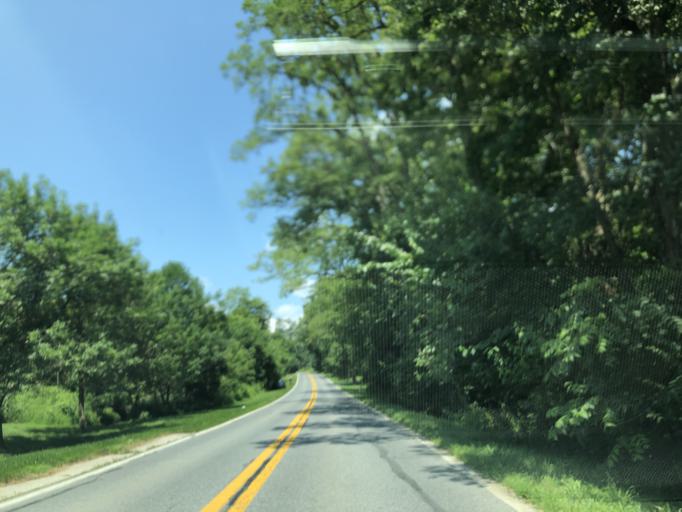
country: US
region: Maryland
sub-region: Carroll County
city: Westminster
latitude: 39.5247
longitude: -76.9517
